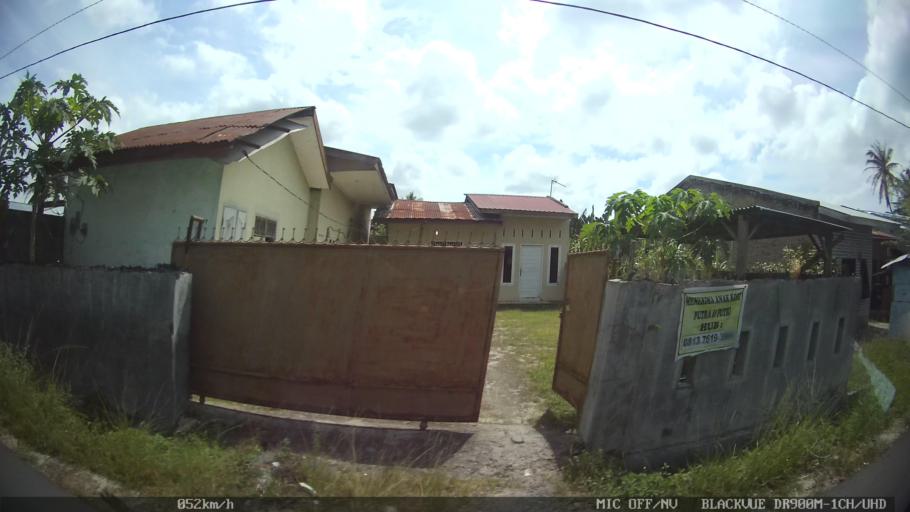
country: ID
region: North Sumatra
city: Percut
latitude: 3.5921
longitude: 98.8614
